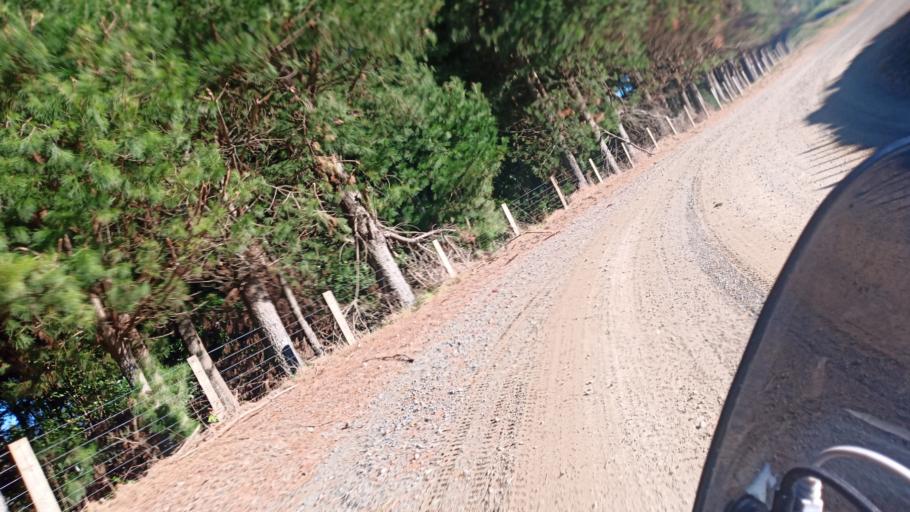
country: NZ
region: Hawke's Bay
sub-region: Wairoa District
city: Wairoa
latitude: -38.7933
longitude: 177.2788
